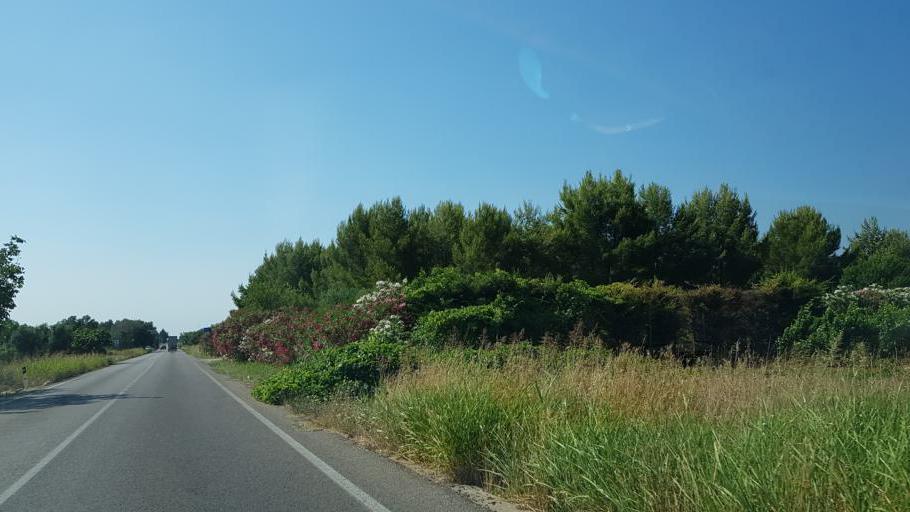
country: IT
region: Apulia
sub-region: Provincia di Lecce
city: Guagnano
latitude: 40.4178
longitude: 17.9539
